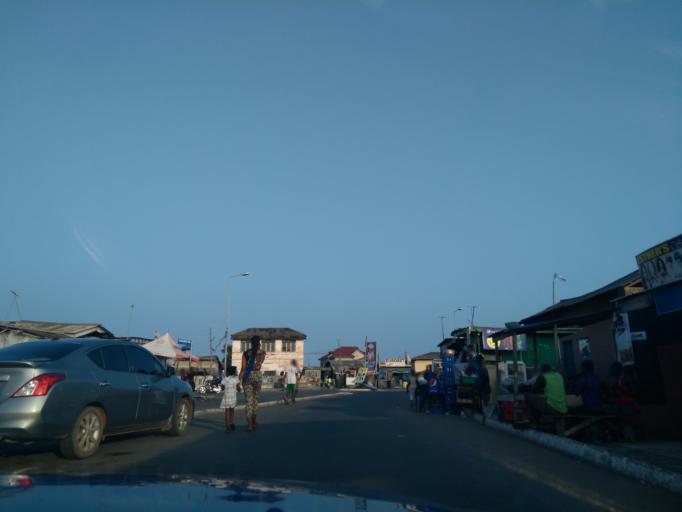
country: GH
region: Greater Accra
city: Accra
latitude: 5.5355
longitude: -0.2134
